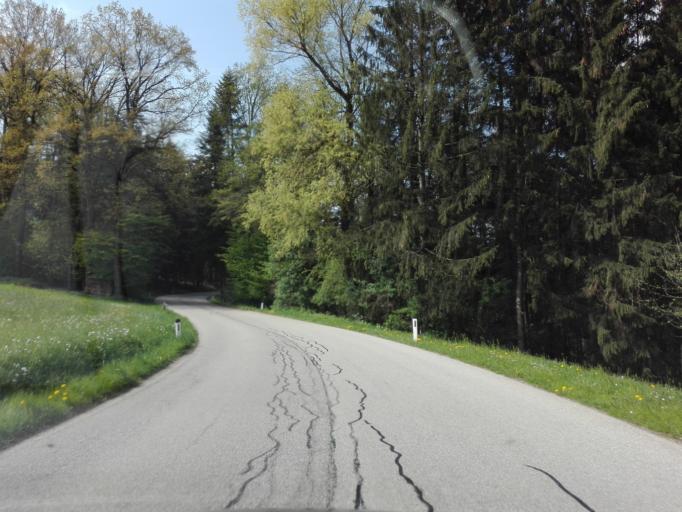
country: AT
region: Upper Austria
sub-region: Politischer Bezirk Perg
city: Perg
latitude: 48.2467
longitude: 14.7034
